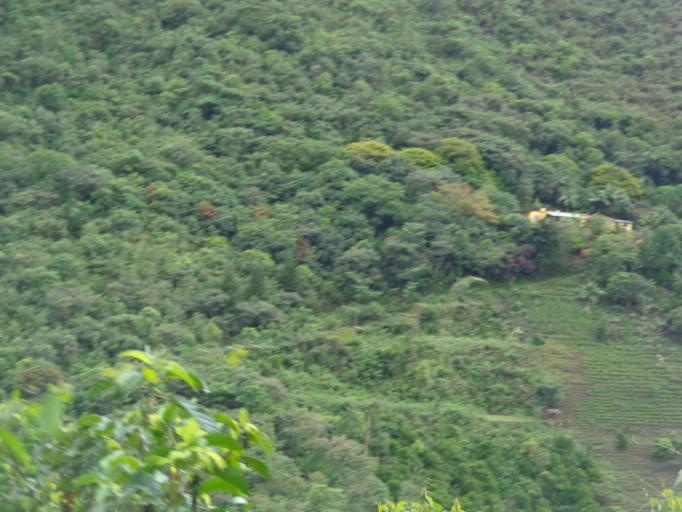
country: BO
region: La Paz
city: Coripata
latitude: -16.3944
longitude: -67.6783
